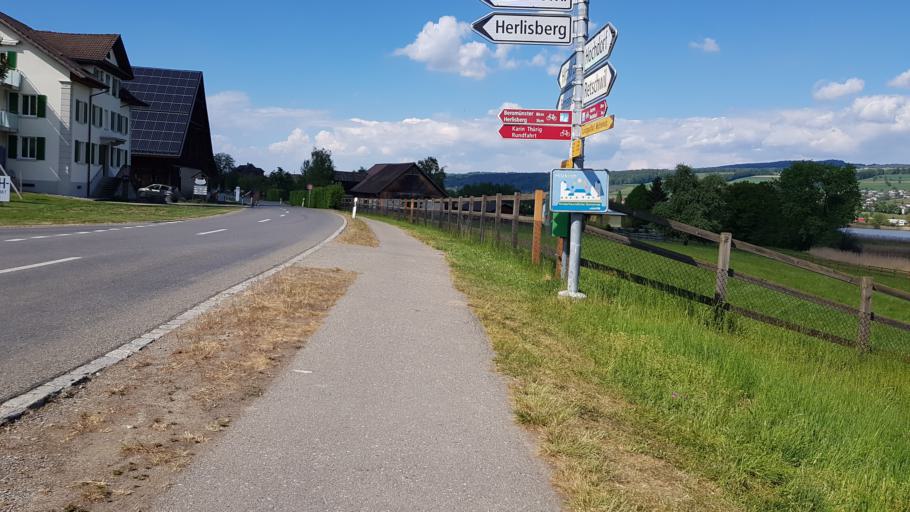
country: CH
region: Lucerne
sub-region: Hochdorf District
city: Hitzkirch
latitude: 47.2098
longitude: 8.2425
